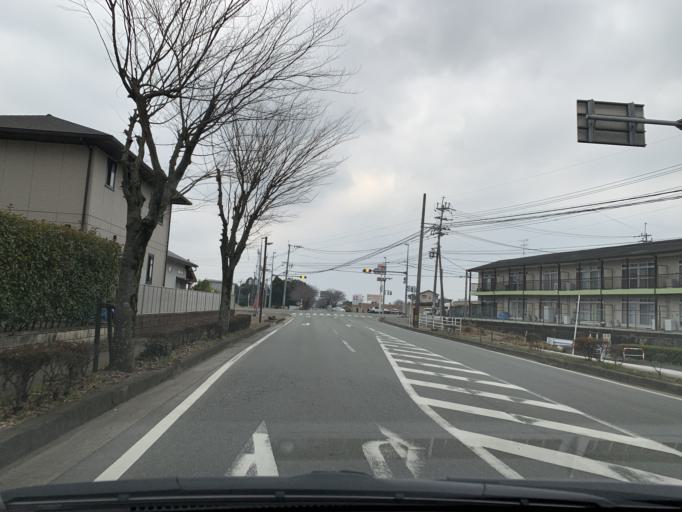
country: JP
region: Kumamoto
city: Ozu
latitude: 32.8891
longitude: 130.8822
